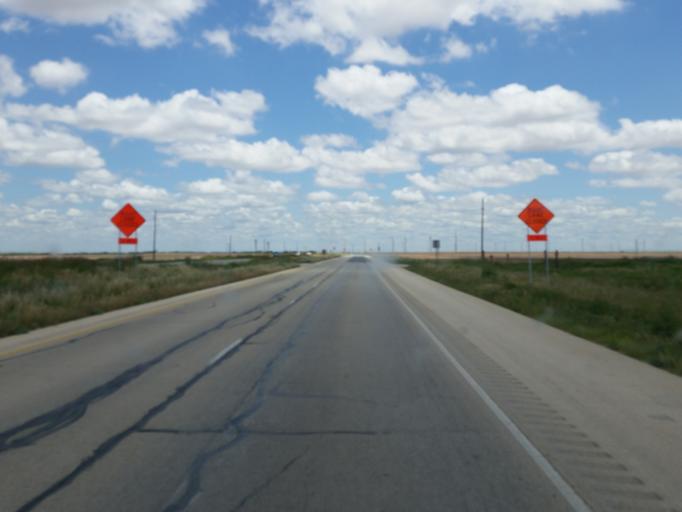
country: US
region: Texas
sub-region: Nolan County
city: Roscoe
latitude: 32.4794
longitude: -100.6171
